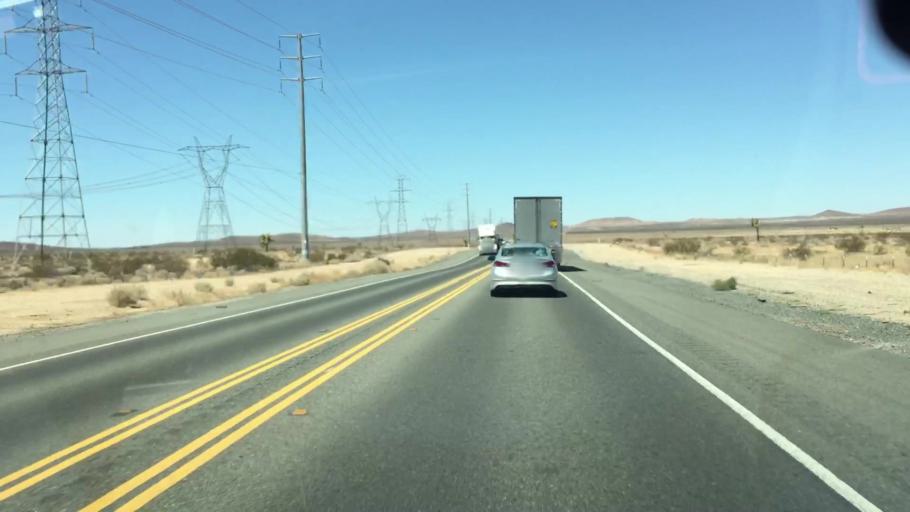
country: US
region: California
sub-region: San Bernardino County
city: Adelanto
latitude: 34.8031
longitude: -117.4884
